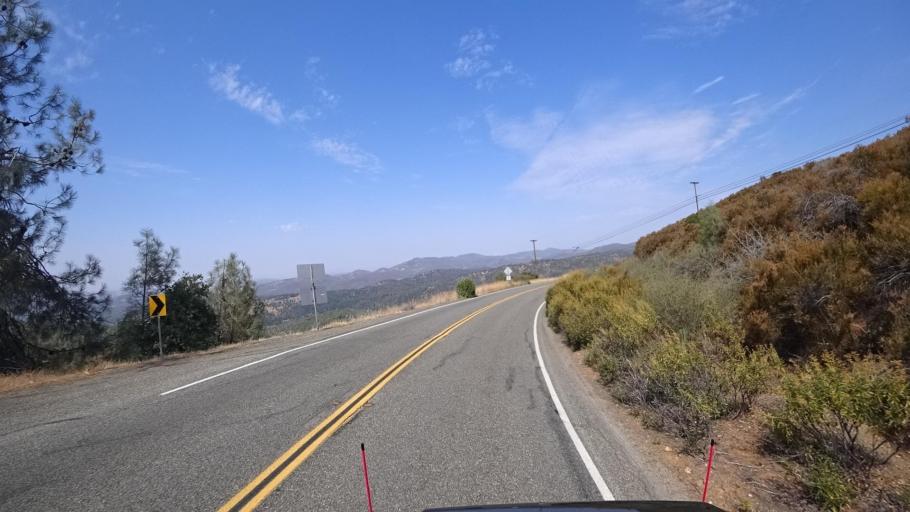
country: US
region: California
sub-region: Tuolumne County
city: Tuolumne City
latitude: 37.7333
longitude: -120.1664
